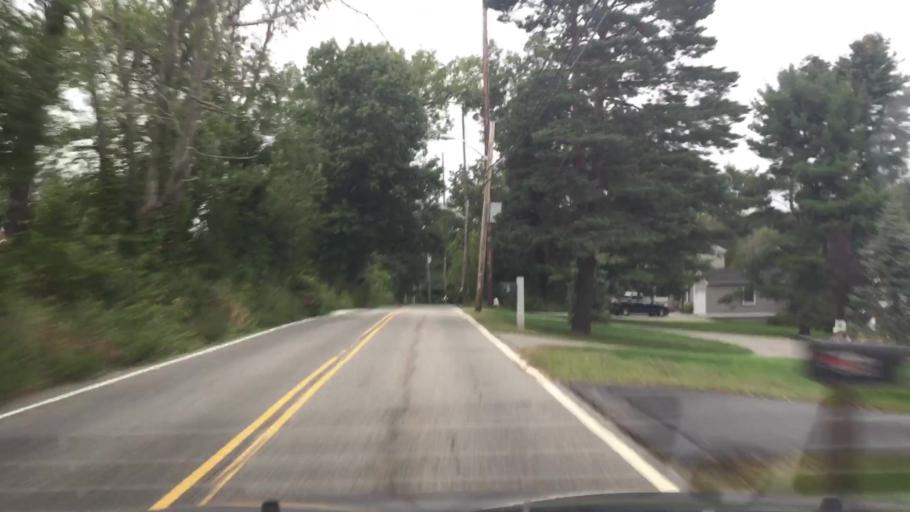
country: US
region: Massachusetts
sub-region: Essex County
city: North Andover
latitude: 42.7285
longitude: -71.1019
